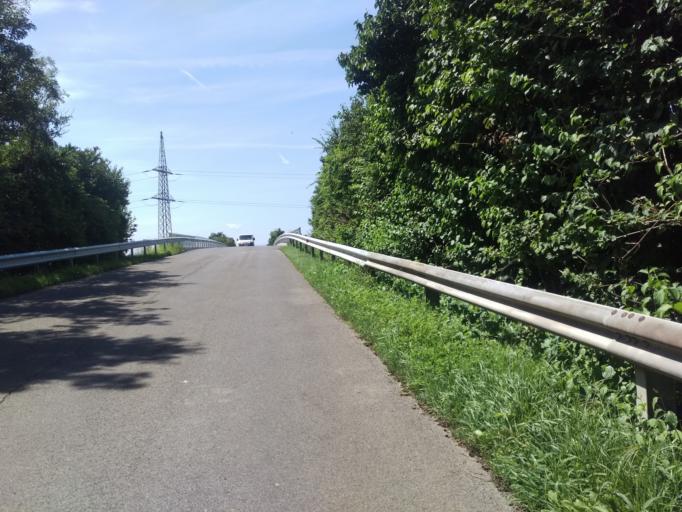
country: AT
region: Styria
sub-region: Politischer Bezirk Graz-Umgebung
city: Seiersberg
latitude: 46.9872
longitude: 15.4170
